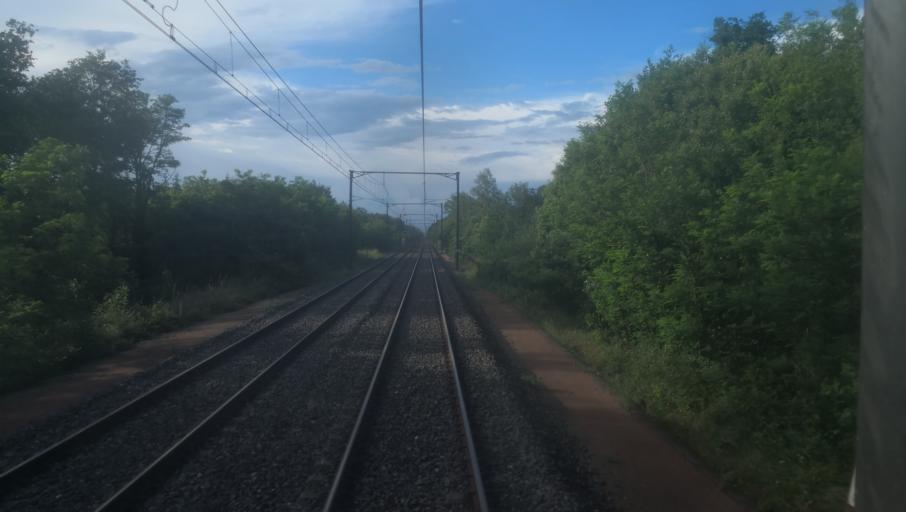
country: FR
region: Centre
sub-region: Departement du Loir-et-Cher
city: Nouan-le-Fuzelier
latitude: 47.4837
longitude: 2.0387
